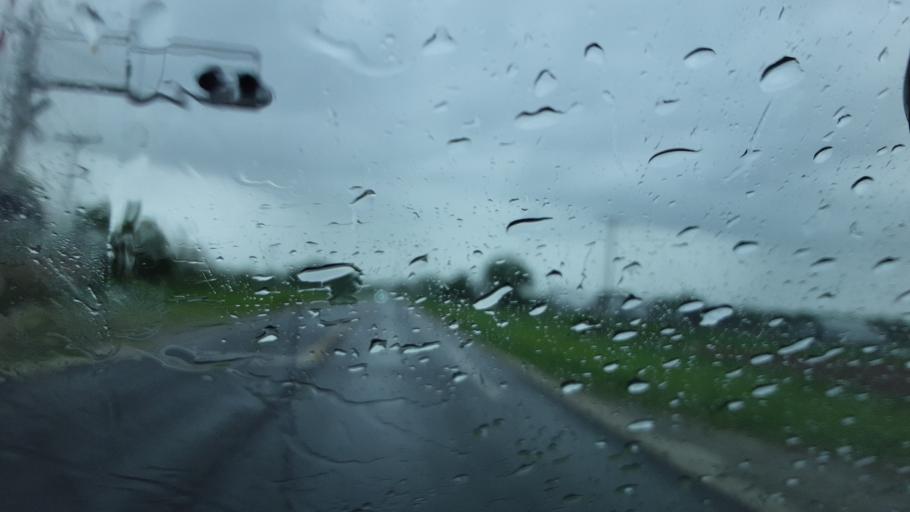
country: US
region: Missouri
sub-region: Monroe County
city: Paris
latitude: 39.4804
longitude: -92.1625
